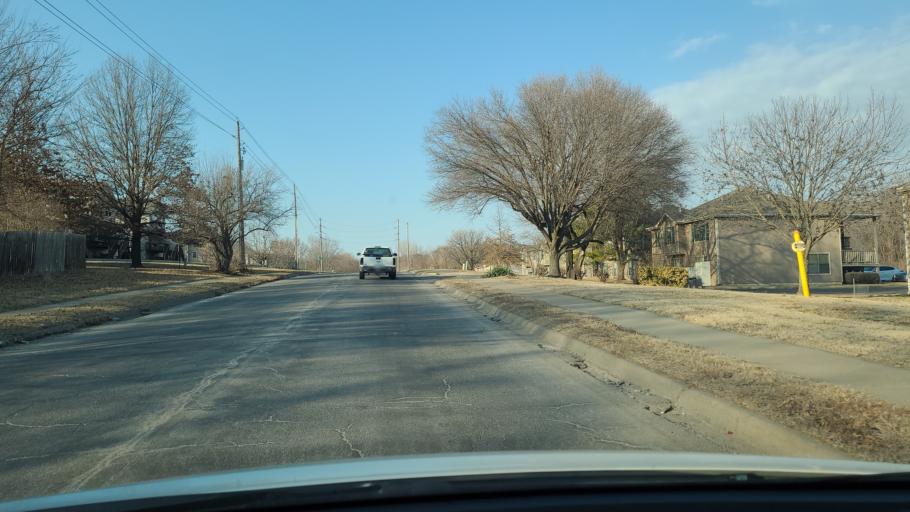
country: US
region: Kansas
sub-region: Douglas County
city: Lawrence
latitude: 38.9656
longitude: -95.2883
